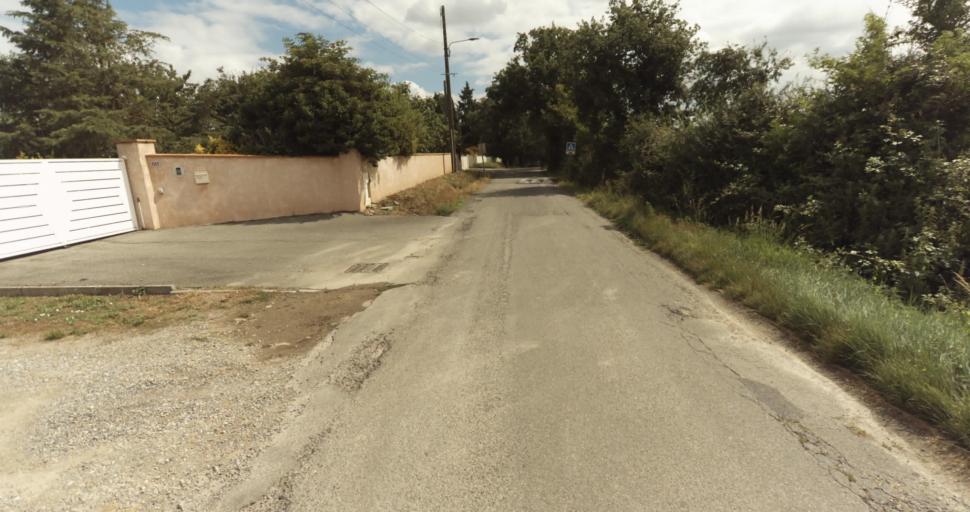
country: FR
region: Midi-Pyrenees
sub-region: Departement de la Haute-Garonne
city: Fontenilles
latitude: 43.5579
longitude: 1.2110
